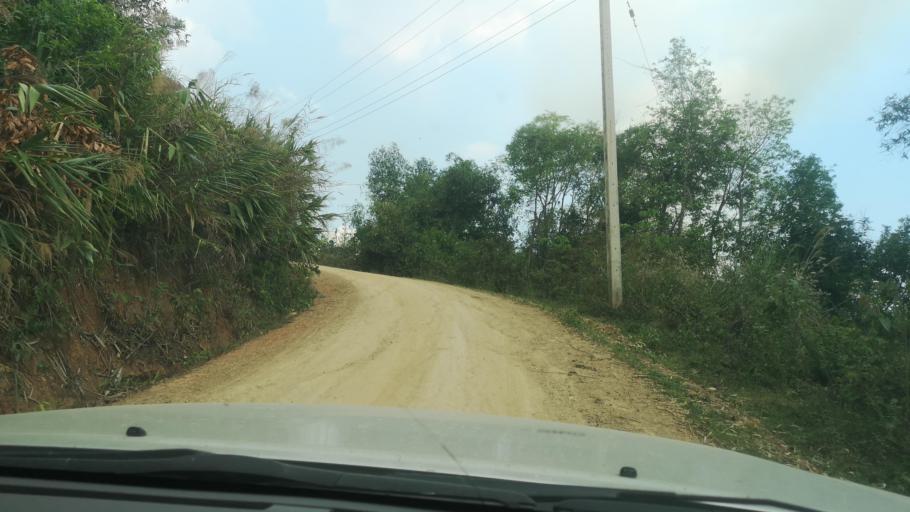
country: LA
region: Loungnamtha
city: Muang Nale
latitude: 20.2904
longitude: 101.3661
